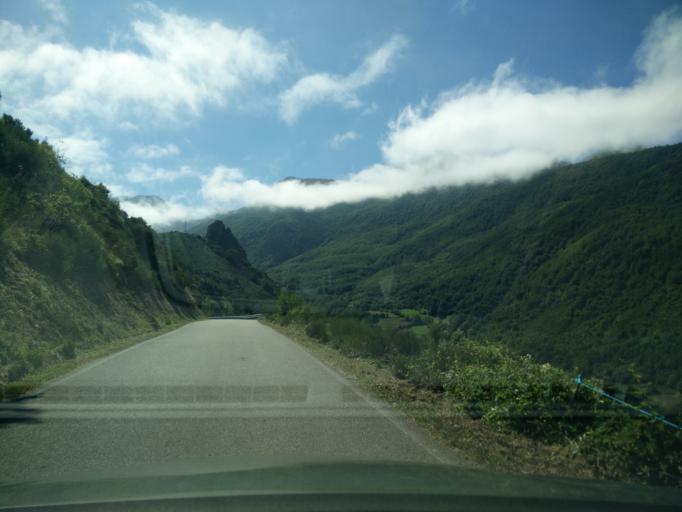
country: ES
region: Asturias
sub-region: Province of Asturias
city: Pola de Somiedo
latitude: 43.0831
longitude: -6.2329
